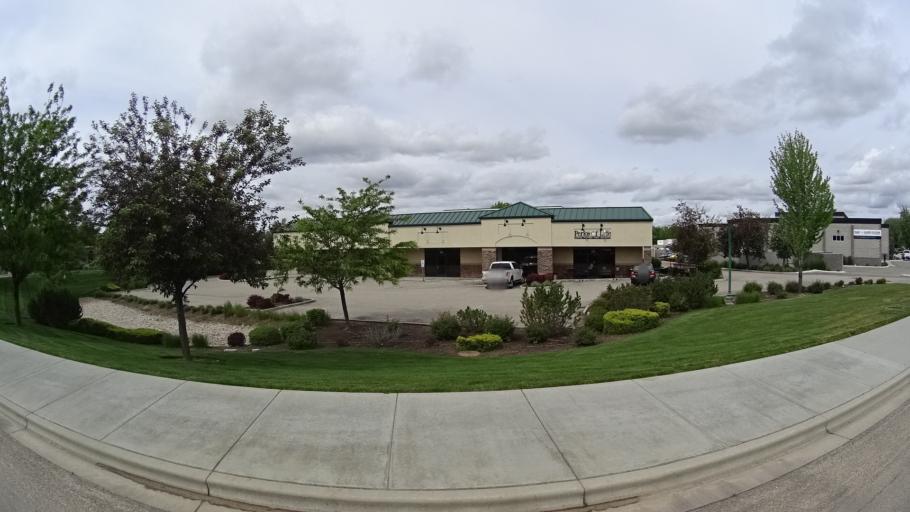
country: US
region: Idaho
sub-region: Ada County
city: Eagle
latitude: 43.6898
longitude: -116.3344
